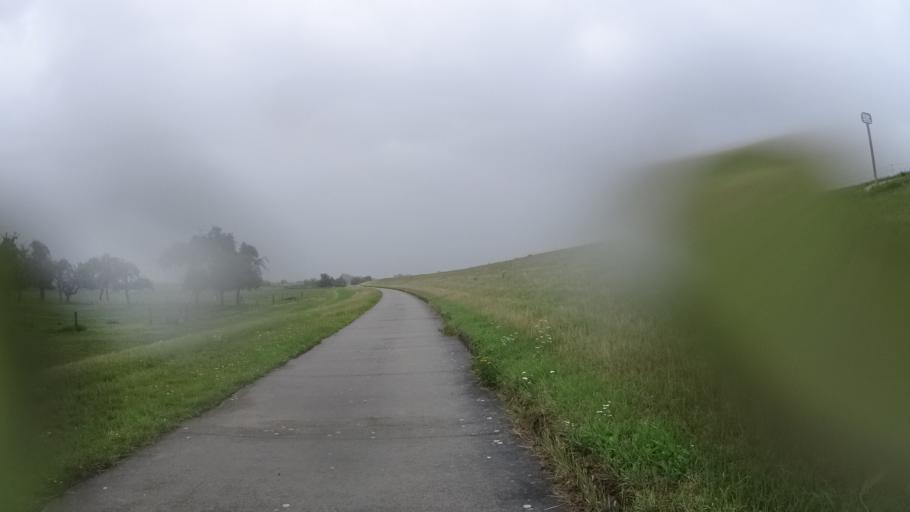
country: DE
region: Lower Saxony
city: Hitzacker
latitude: 53.1811
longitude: 11.0192
